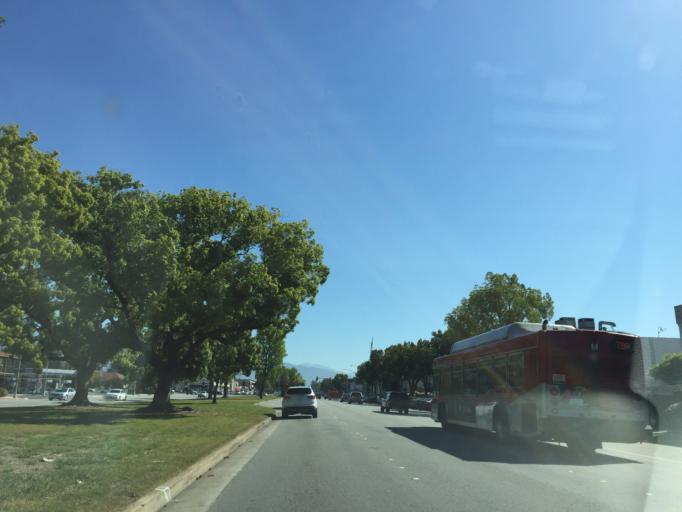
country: US
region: California
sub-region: Los Angeles County
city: San Marino
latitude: 34.1210
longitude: -118.1084
